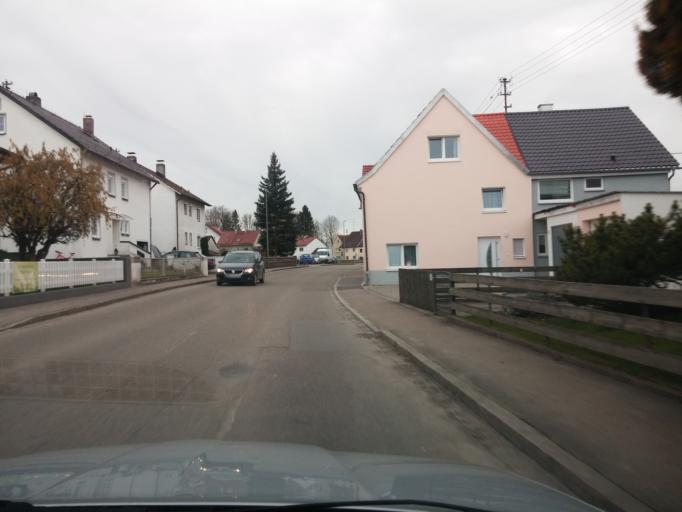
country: DE
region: Bavaria
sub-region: Swabia
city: Trunkelsberg
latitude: 48.0043
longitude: 10.2211
